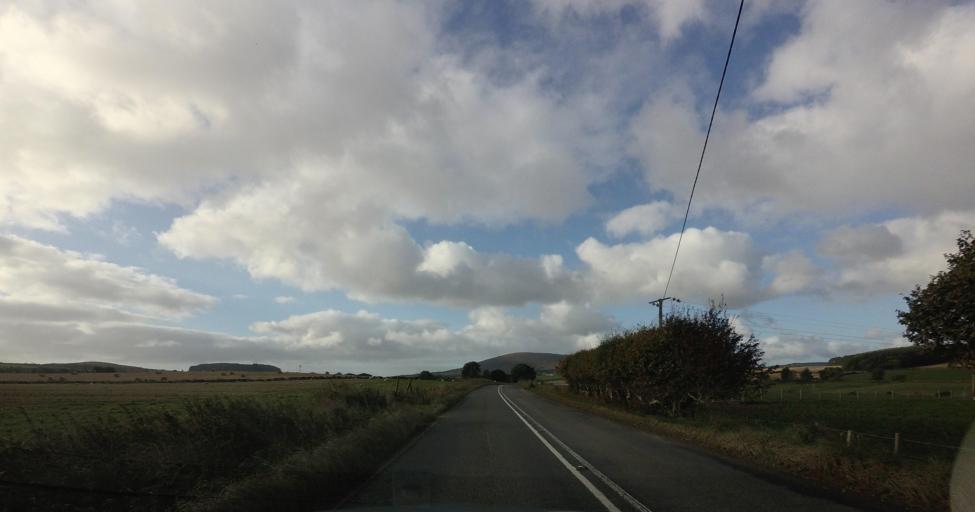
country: GB
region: Scotland
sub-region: Aberdeenshire
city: Portsoy
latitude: 57.6031
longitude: -2.7170
